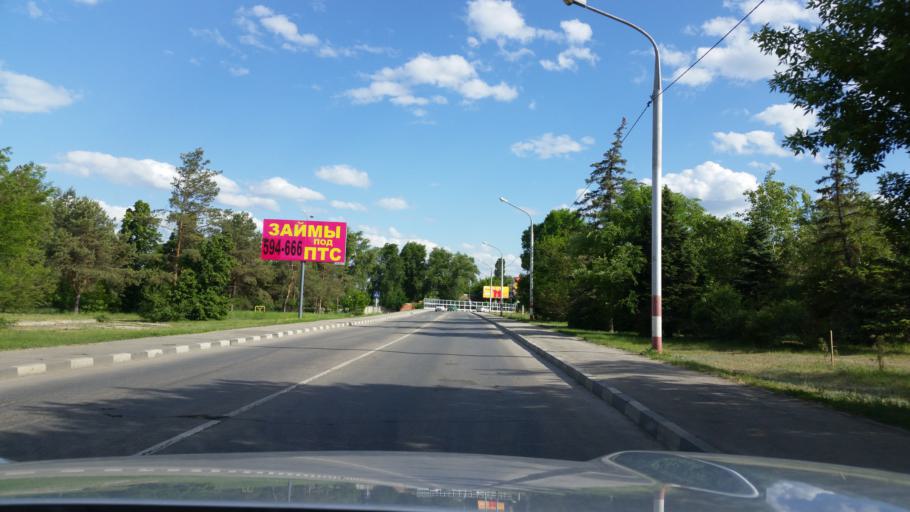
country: RU
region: Saratov
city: Engel's
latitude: 51.5044
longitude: 46.0796
